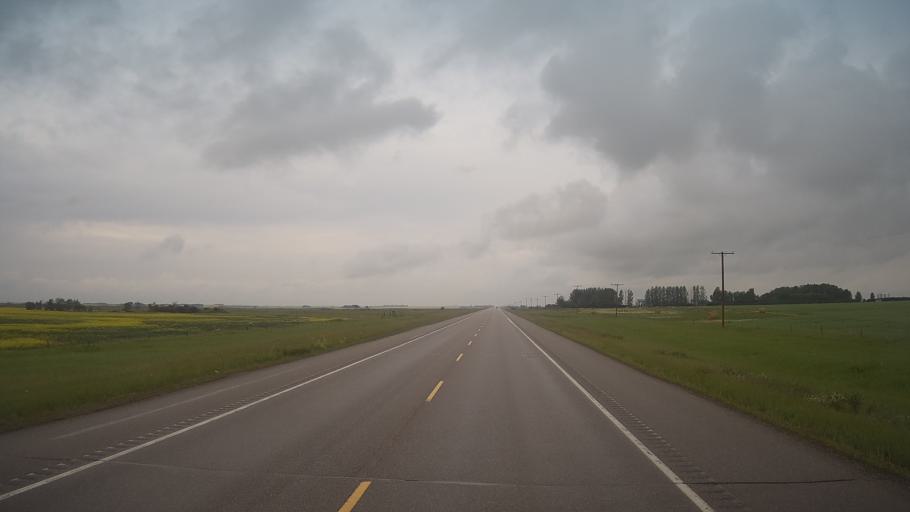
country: CA
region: Saskatchewan
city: Unity
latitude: 52.4349
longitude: -108.9674
